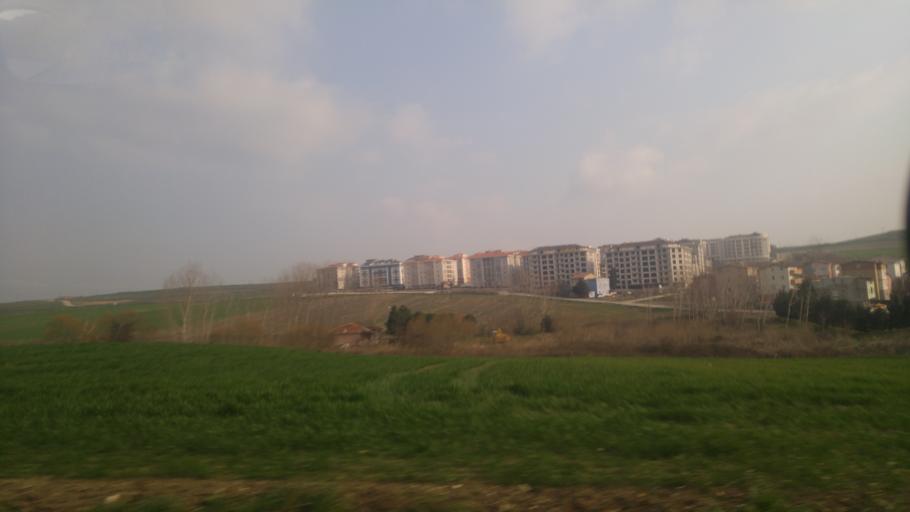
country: TR
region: Istanbul
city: Silivri
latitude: 41.0865
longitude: 28.2673
